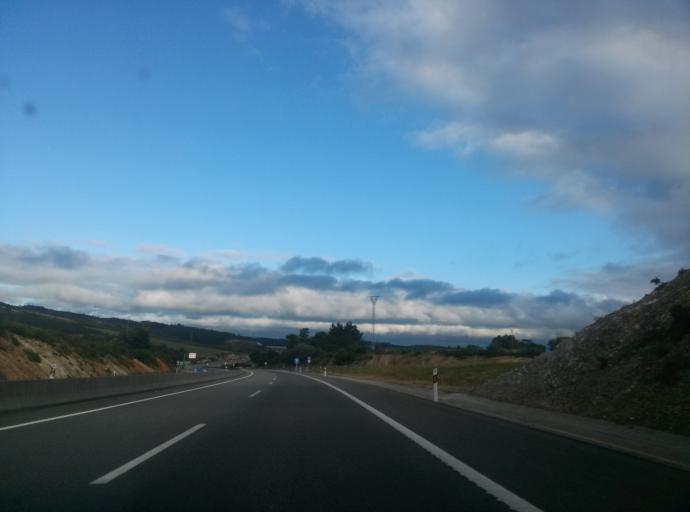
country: ES
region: Galicia
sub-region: Provincia de Lugo
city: Vilalba
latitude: 43.3533
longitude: -7.7452
